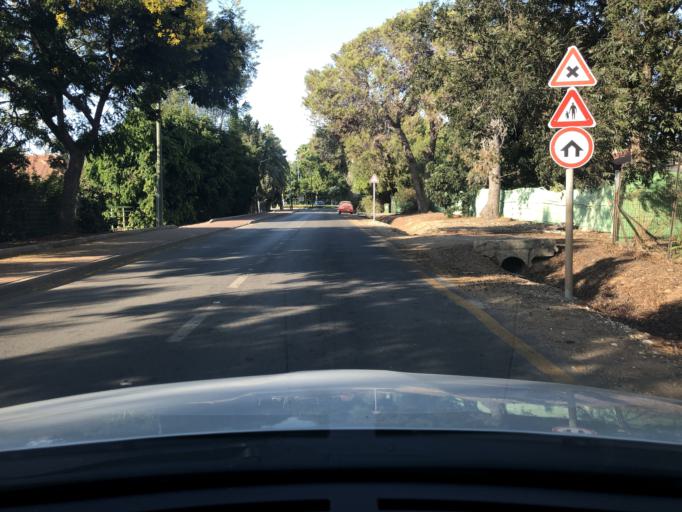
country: IL
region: Central District
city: Hod HaSharon
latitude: 32.1381
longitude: 34.9078
